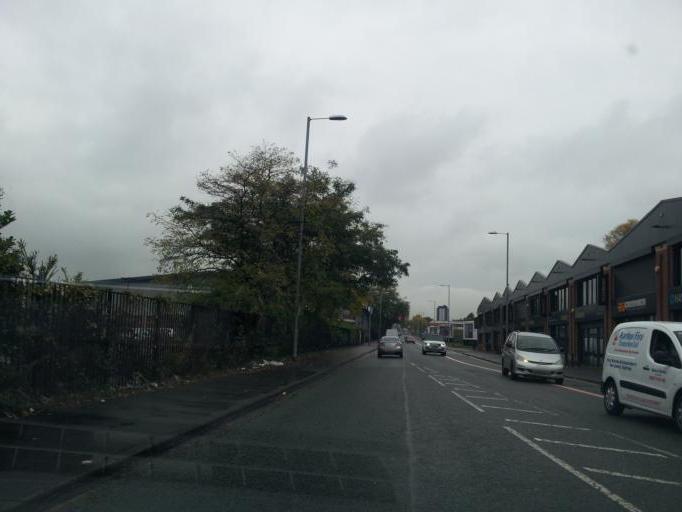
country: GB
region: England
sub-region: Manchester
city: Cheetham Hill
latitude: 53.4954
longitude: -2.2517
